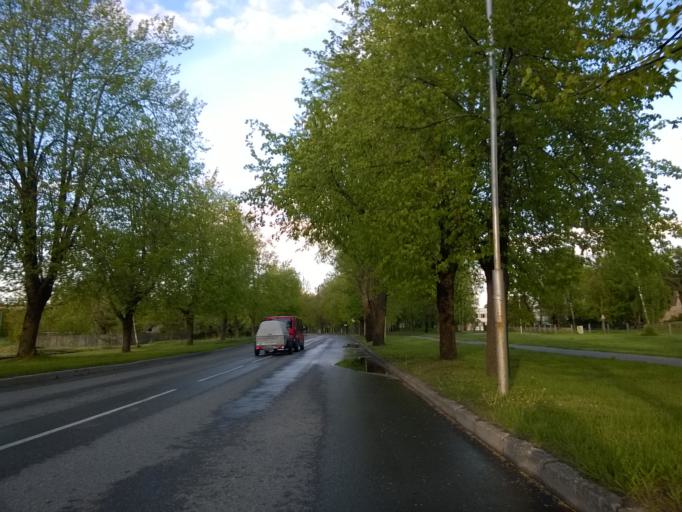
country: LV
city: Tireli
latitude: 56.9476
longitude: 23.6237
